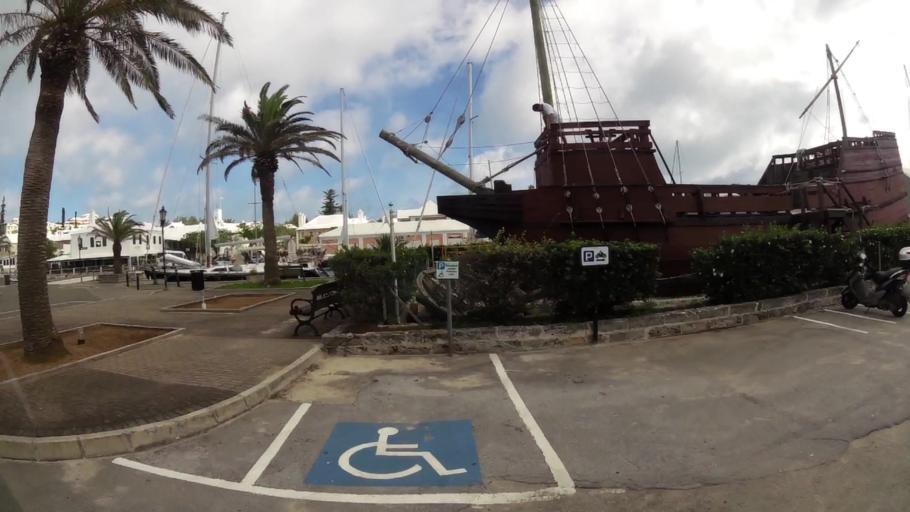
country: BM
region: Saint George
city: Saint George
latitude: 32.3802
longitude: -64.6764
